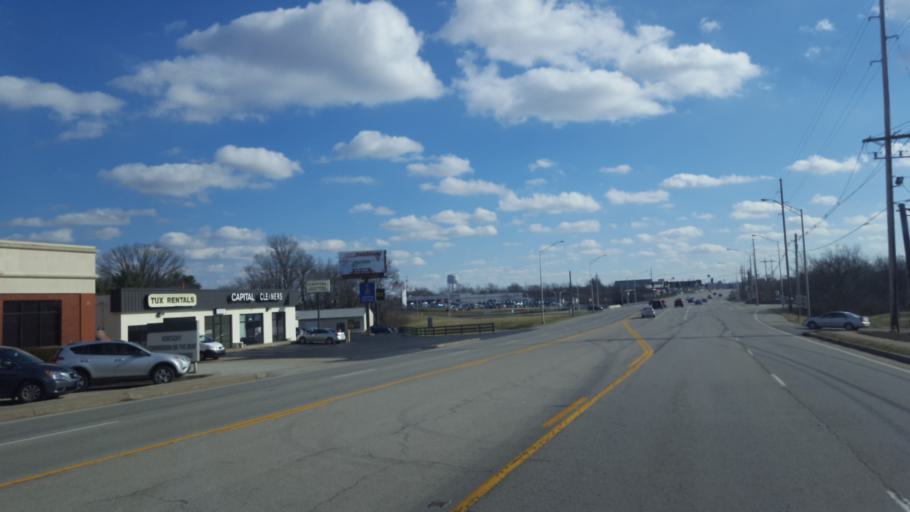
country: US
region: Kentucky
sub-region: Franklin County
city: Frankfort
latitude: 38.1904
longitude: -84.8233
